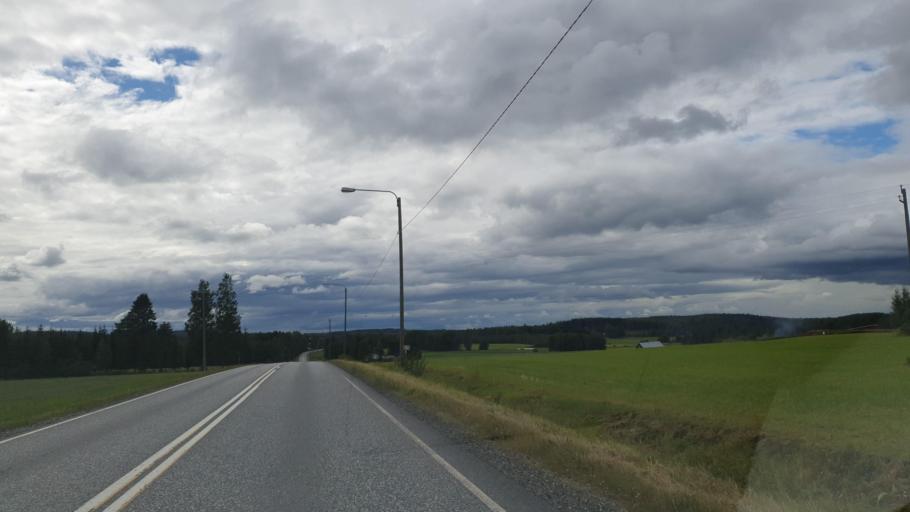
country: FI
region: Northern Savo
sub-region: Ylae-Savo
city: Iisalmi
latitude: 63.5210
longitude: 27.1701
